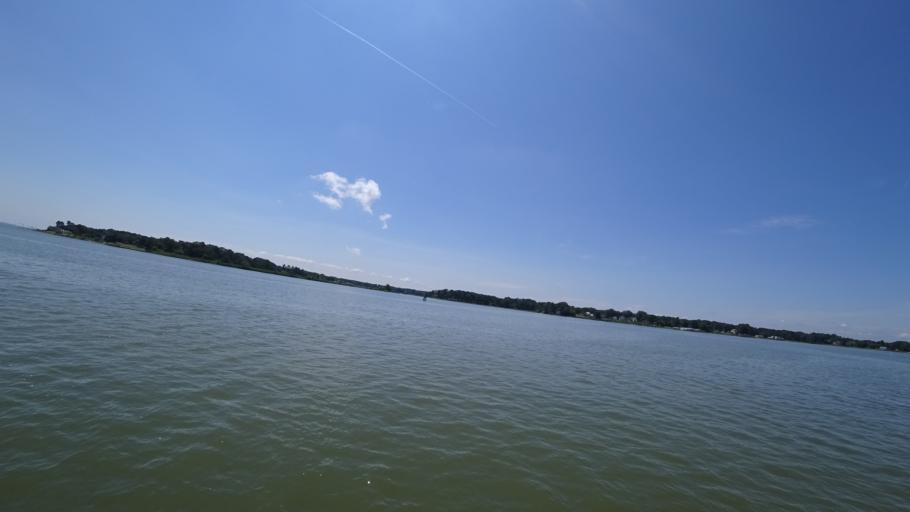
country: US
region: Virginia
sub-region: Isle of Wight County
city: Carrollton
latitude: 37.0050
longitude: -76.5742
